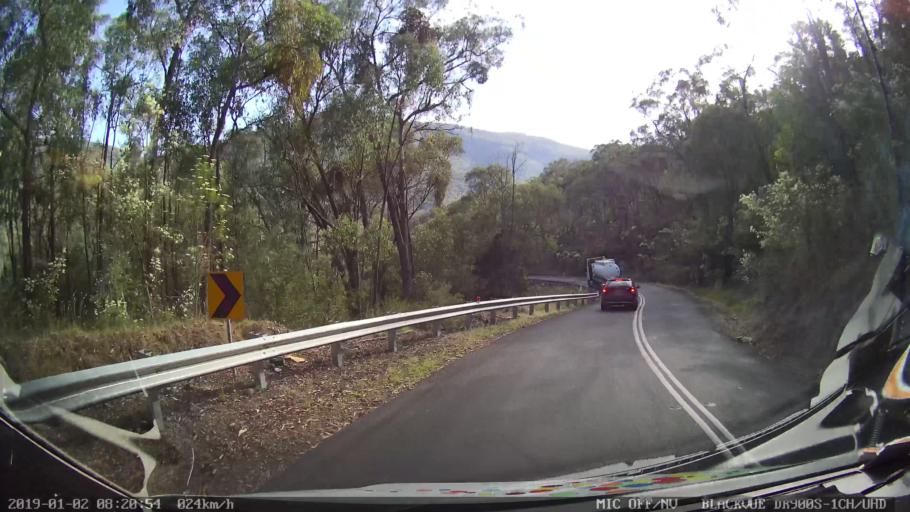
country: AU
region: New South Wales
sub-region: Tumut Shire
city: Tumut
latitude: -35.5710
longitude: 148.3242
